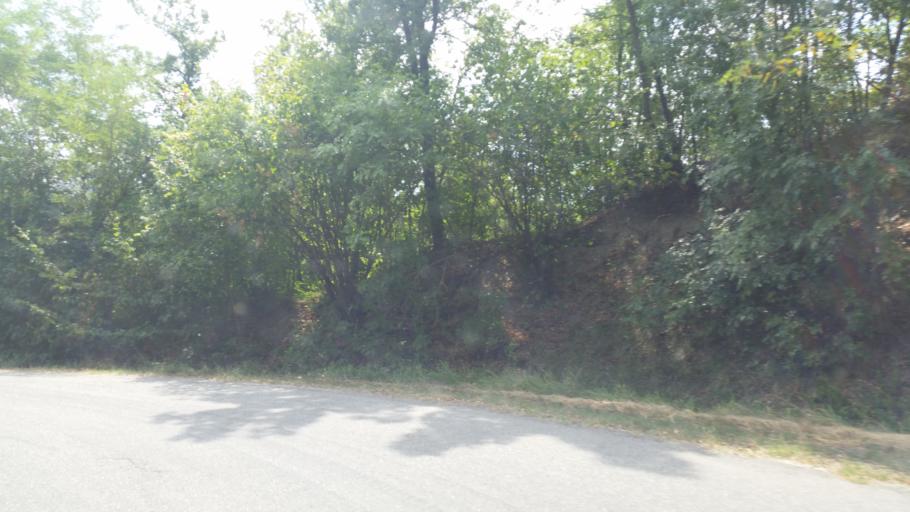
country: IT
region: Piedmont
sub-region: Provincia di Asti
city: Vesime
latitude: 44.6373
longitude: 8.2356
